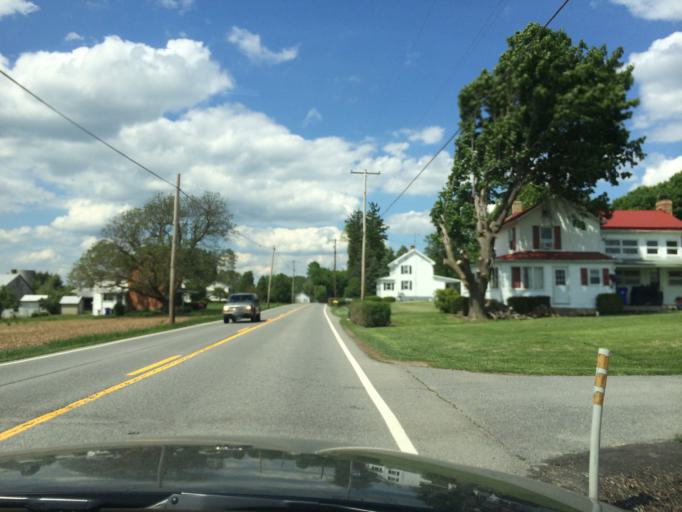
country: US
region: Maryland
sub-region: Frederick County
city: Woodsboro
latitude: 39.5248
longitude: -77.2351
